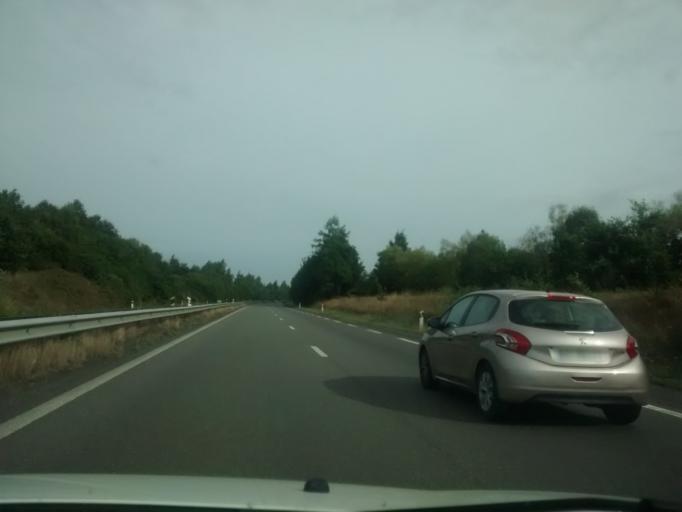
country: FR
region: Brittany
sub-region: Departement d'Ille-et-Vilaine
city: Hede-Bazouges
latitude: 48.2750
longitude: -1.7895
